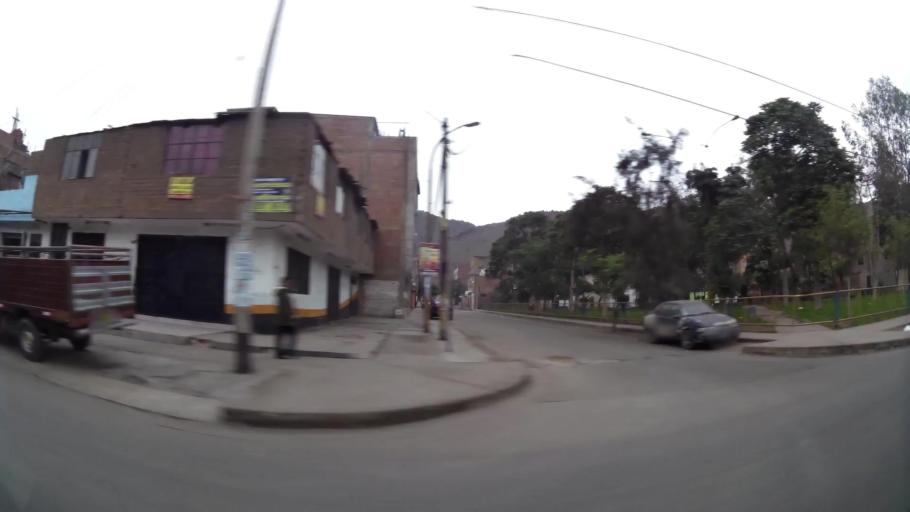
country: PE
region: Lima
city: Lima
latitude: -12.0198
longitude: -76.9846
